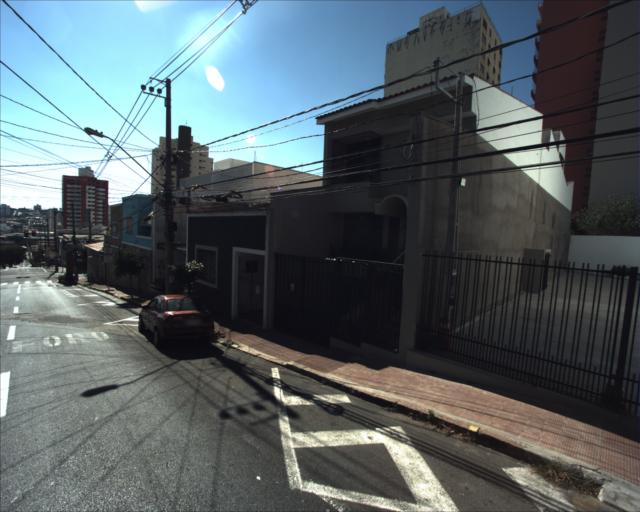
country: BR
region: Sao Paulo
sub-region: Sorocaba
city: Sorocaba
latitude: -23.5017
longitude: -47.4646
